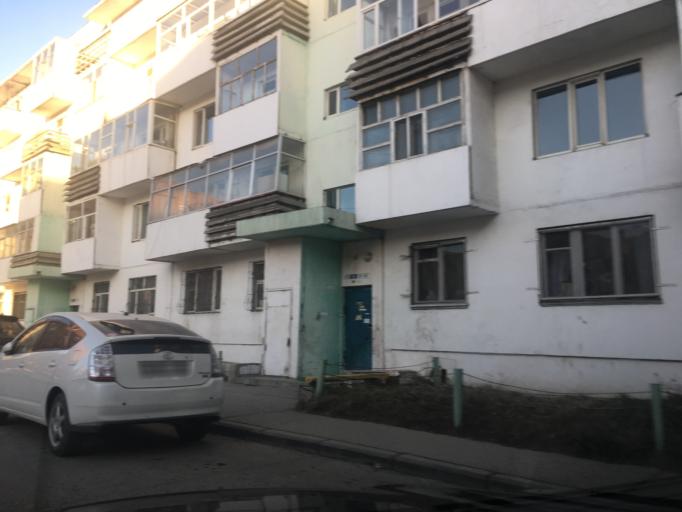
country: MN
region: Ulaanbaatar
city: Ulaanbaatar
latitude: 47.9190
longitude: 106.8832
